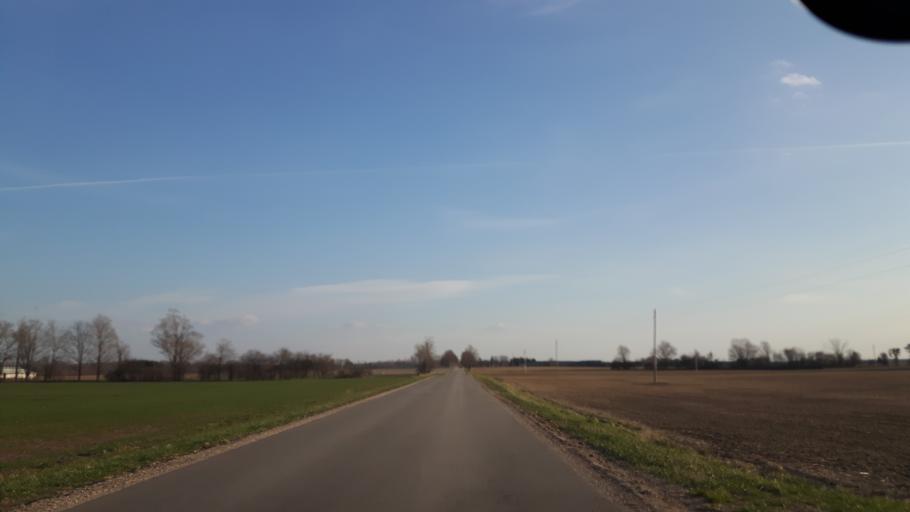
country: CA
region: Ontario
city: Goderich
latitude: 43.6354
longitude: -81.6644
